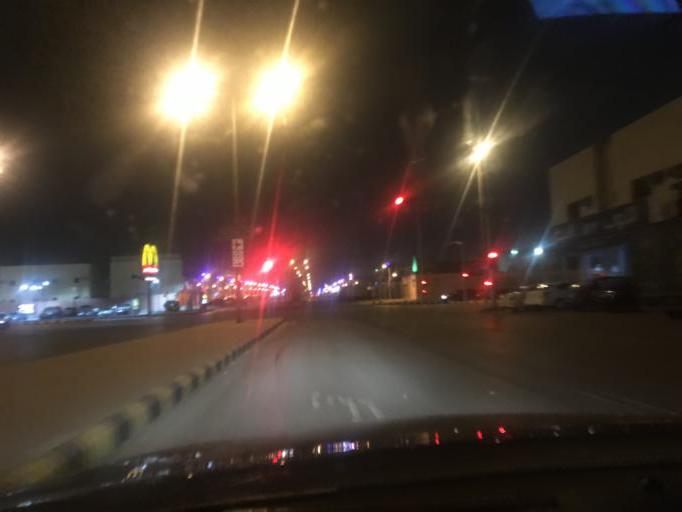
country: SA
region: Ar Riyad
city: Riyadh
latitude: 24.7622
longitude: 46.7979
